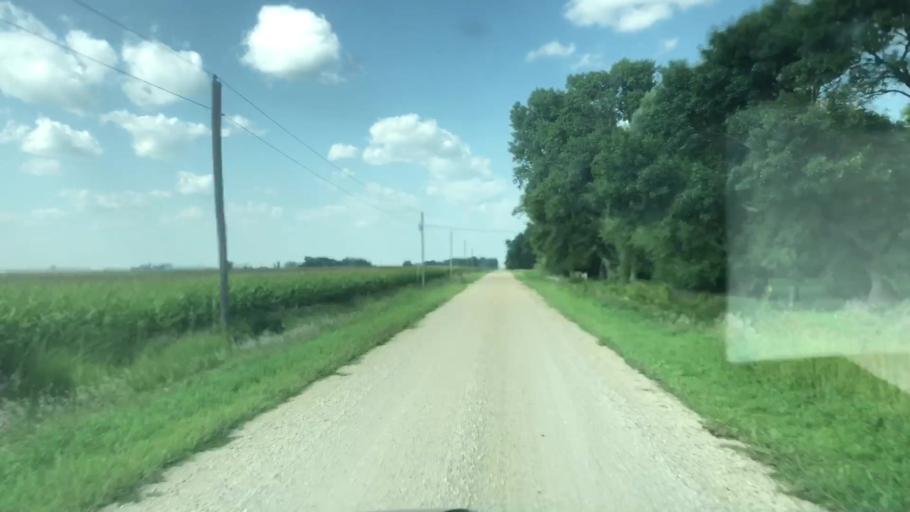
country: US
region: Iowa
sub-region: O'Brien County
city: Sheldon
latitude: 43.1621
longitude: -95.7822
